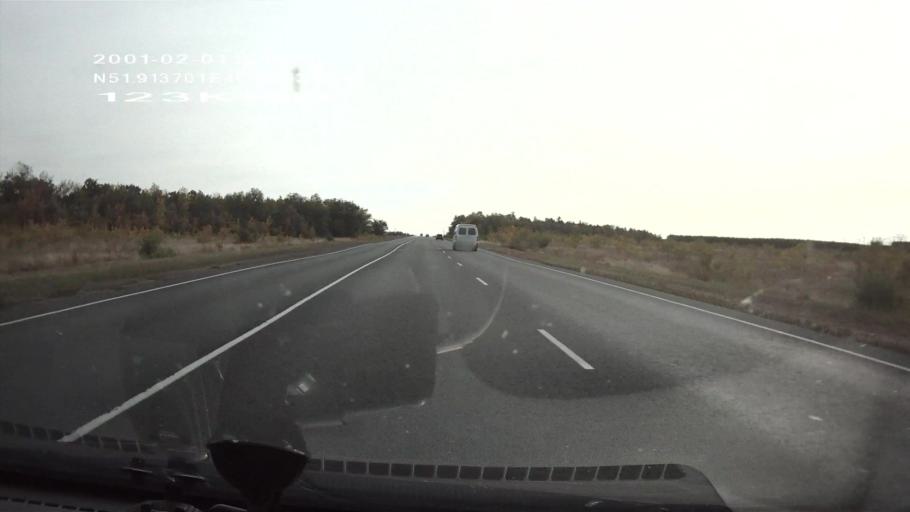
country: RU
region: Saratov
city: Sinodskoye
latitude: 51.9124
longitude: 46.5544
